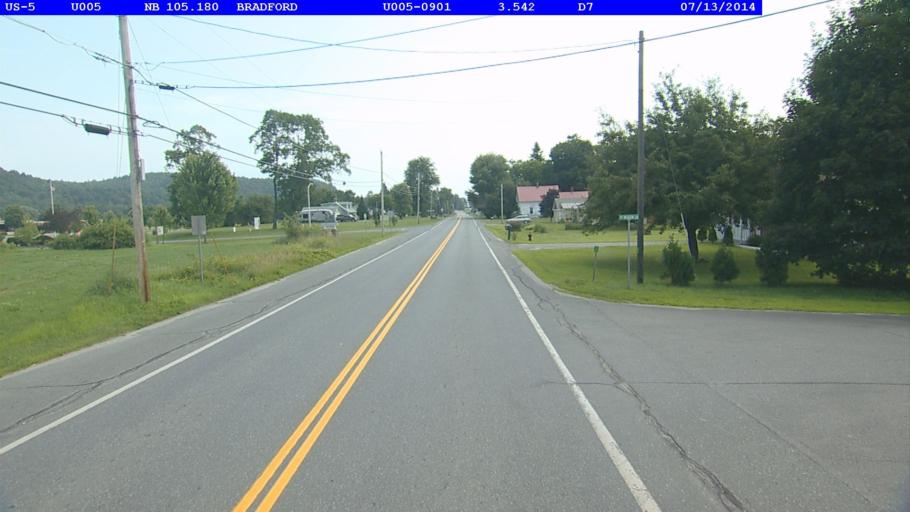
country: US
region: New Hampshire
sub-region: Grafton County
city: Haverhill
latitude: 44.0054
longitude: -72.1135
